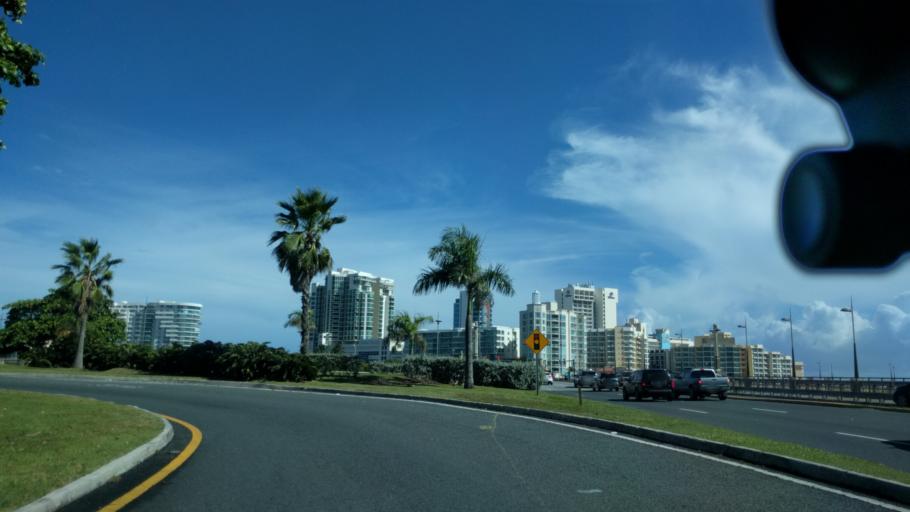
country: PR
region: San Juan
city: San Juan
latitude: 18.4583
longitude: -66.0863
